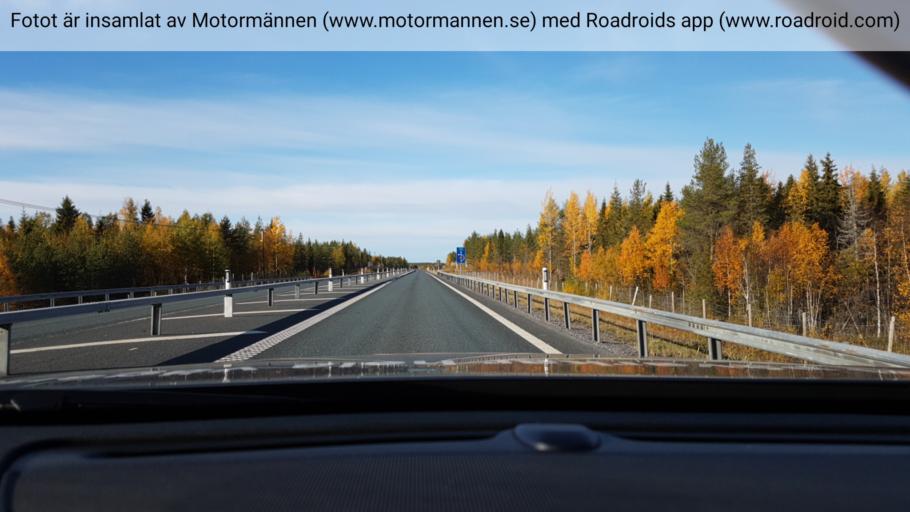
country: SE
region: Norrbotten
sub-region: Kalix Kommun
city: Kalix
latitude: 65.8287
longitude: 23.3839
